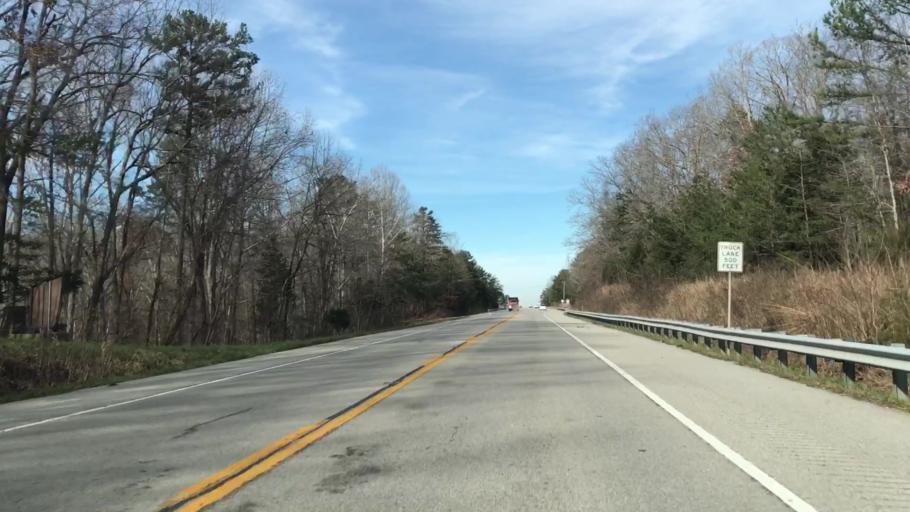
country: US
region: Kentucky
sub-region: Pulaski County
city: Somerset
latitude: 36.9188
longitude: -84.5175
